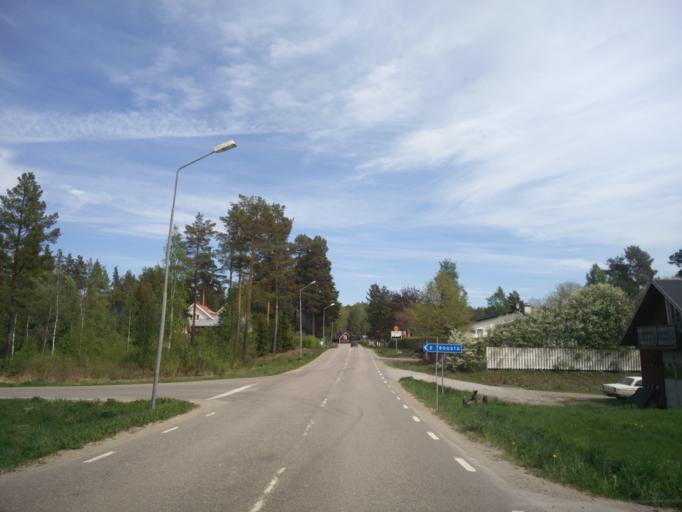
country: SE
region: Gaevleborg
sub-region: Hudiksvalls Kommun
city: Sorforsa
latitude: 61.7099
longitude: 16.9520
